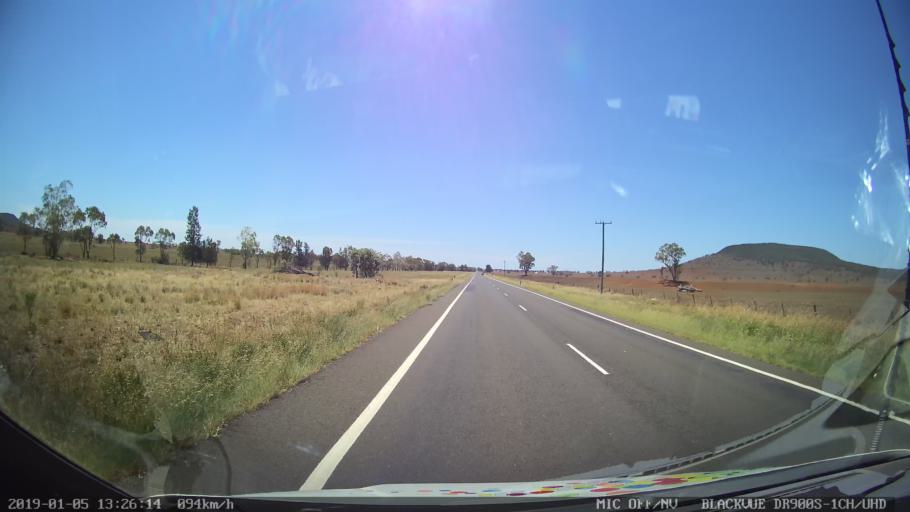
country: AU
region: New South Wales
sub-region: Gunnedah
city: Gunnedah
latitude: -31.0546
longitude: 150.0129
